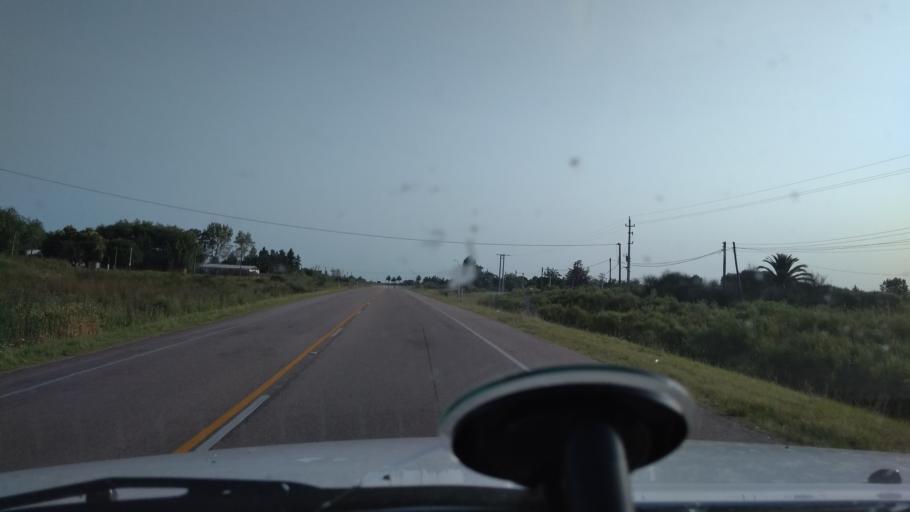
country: UY
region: Canelones
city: Sauce
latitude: -34.6571
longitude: -56.0553
